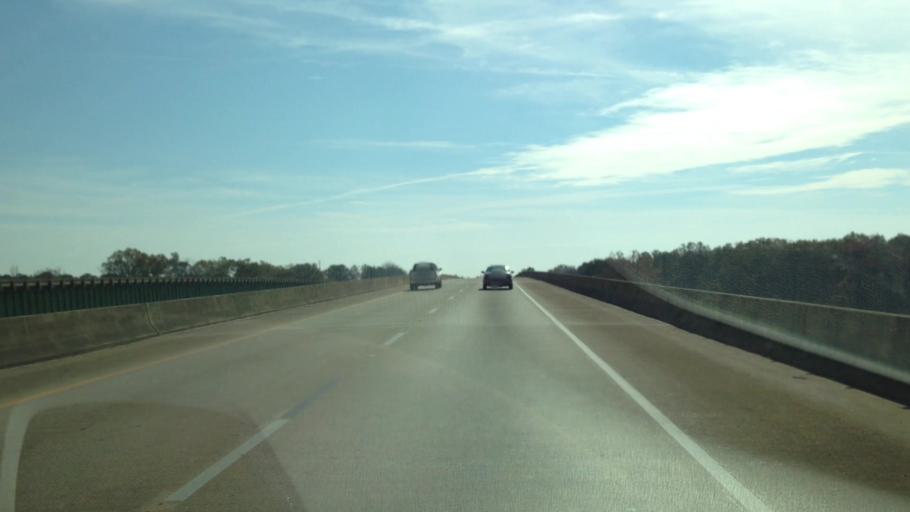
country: US
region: Alabama
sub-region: Autauga County
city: Prattville
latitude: 32.4132
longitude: -86.4090
